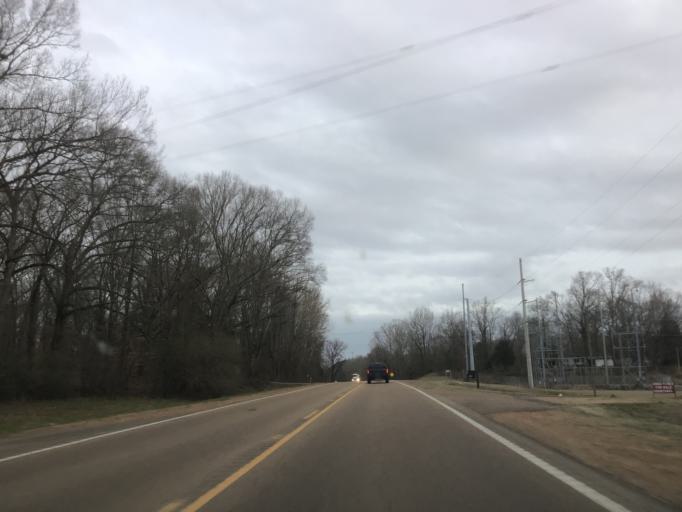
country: US
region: Mississippi
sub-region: Warren County
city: Beechwood
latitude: 32.3136
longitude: -90.8093
